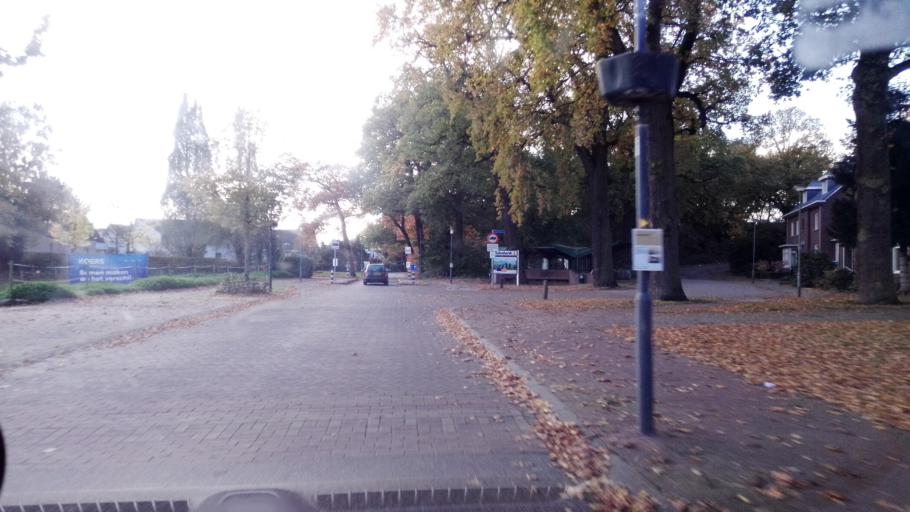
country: NL
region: Limburg
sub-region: Gemeente Venlo
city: Venlo
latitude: 51.4169
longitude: 6.1494
